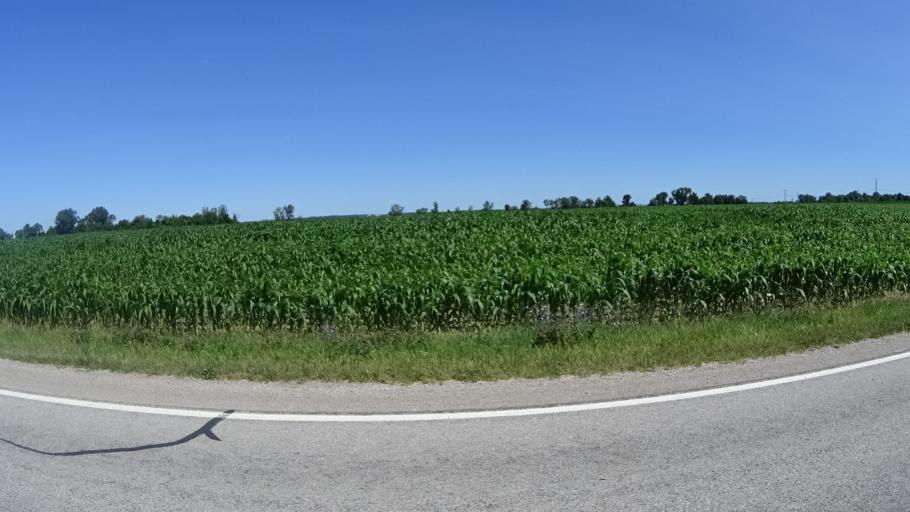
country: US
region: Ohio
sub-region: Ottawa County
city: Port Clinton
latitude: 41.4376
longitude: -82.8545
